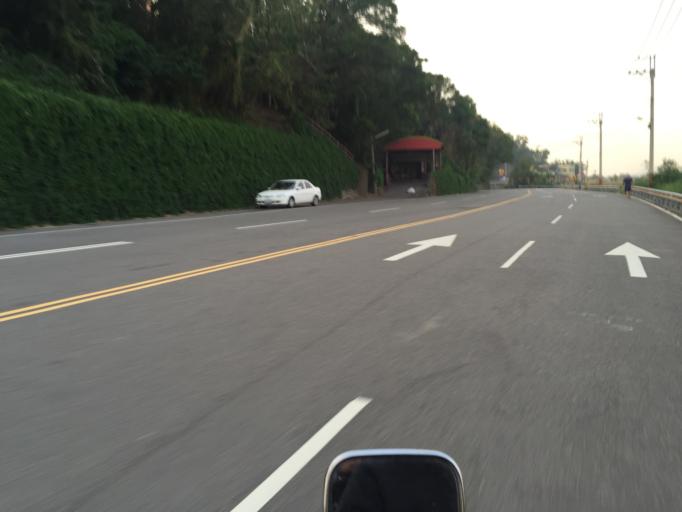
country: TW
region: Taiwan
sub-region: Miaoli
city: Miaoli
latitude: 24.4776
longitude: 120.7772
